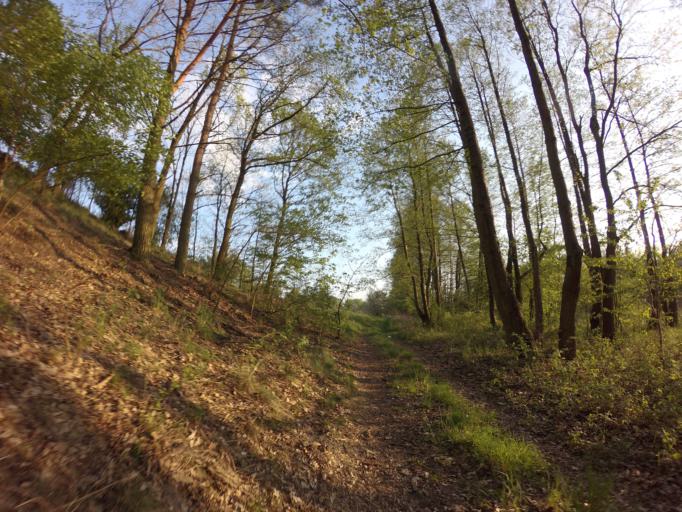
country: PL
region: West Pomeranian Voivodeship
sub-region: Powiat choszczenski
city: Choszczno
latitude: 53.1482
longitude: 15.3469
